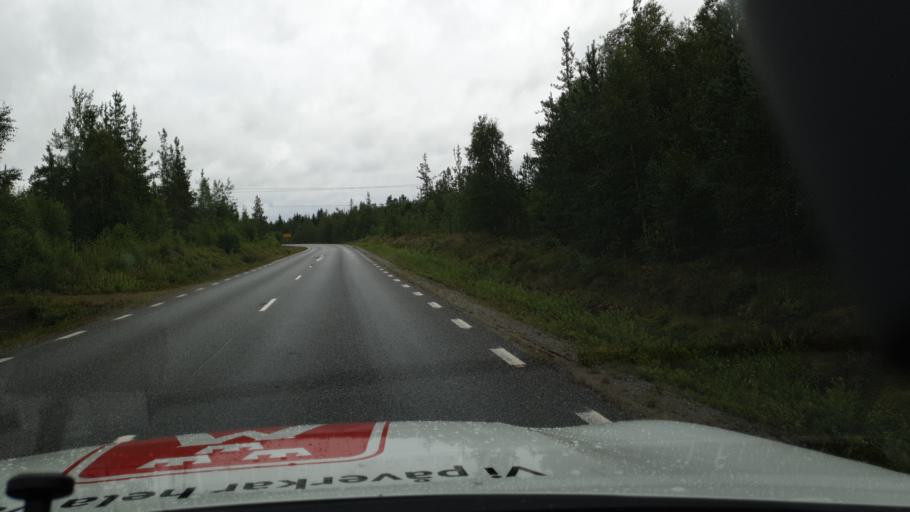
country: SE
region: Vaesterbotten
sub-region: Umea Kommun
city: Saevar
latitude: 63.9159
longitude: 20.5373
